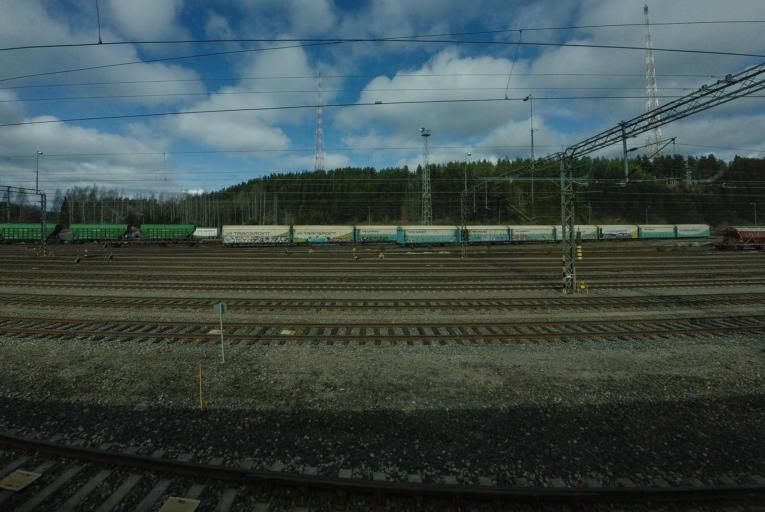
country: FI
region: Paijanne Tavastia
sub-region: Lahti
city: Lahti
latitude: 60.9768
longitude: 25.6438
